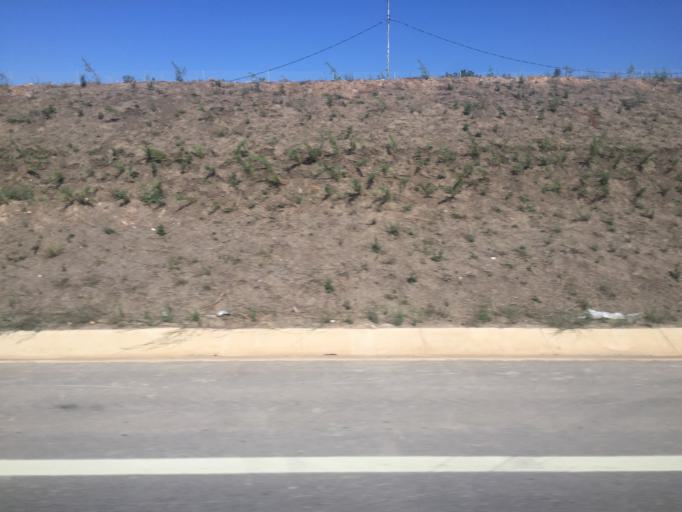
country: TR
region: Bursa
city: Karacabey
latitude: 40.2425
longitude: 28.4312
